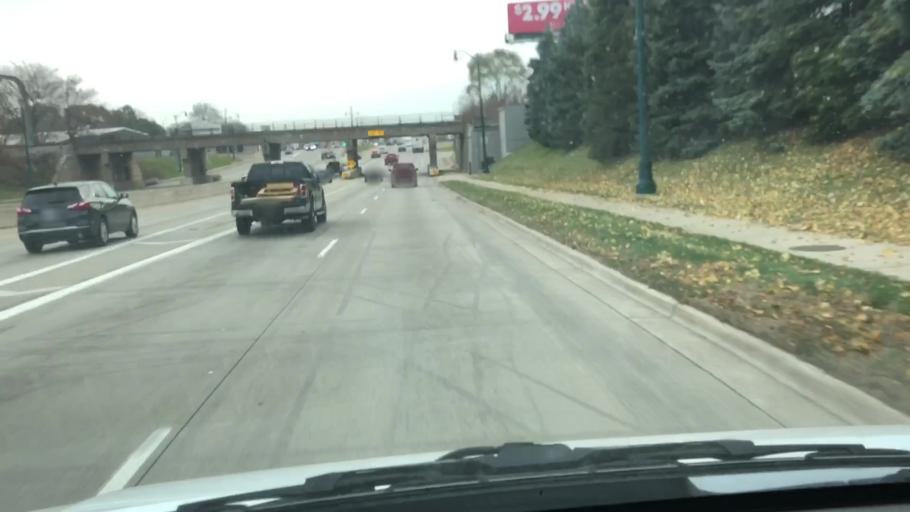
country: US
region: Michigan
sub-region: Wayne County
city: Allen Park
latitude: 42.2612
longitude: -83.2139
